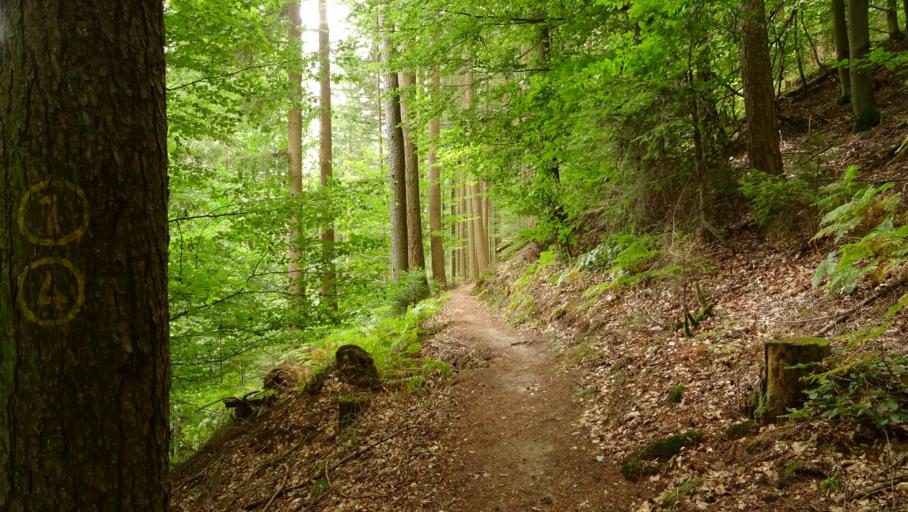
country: DE
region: Baden-Wuerttemberg
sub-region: Karlsruhe Region
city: Neunkirchen
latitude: 49.4224
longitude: 8.9966
